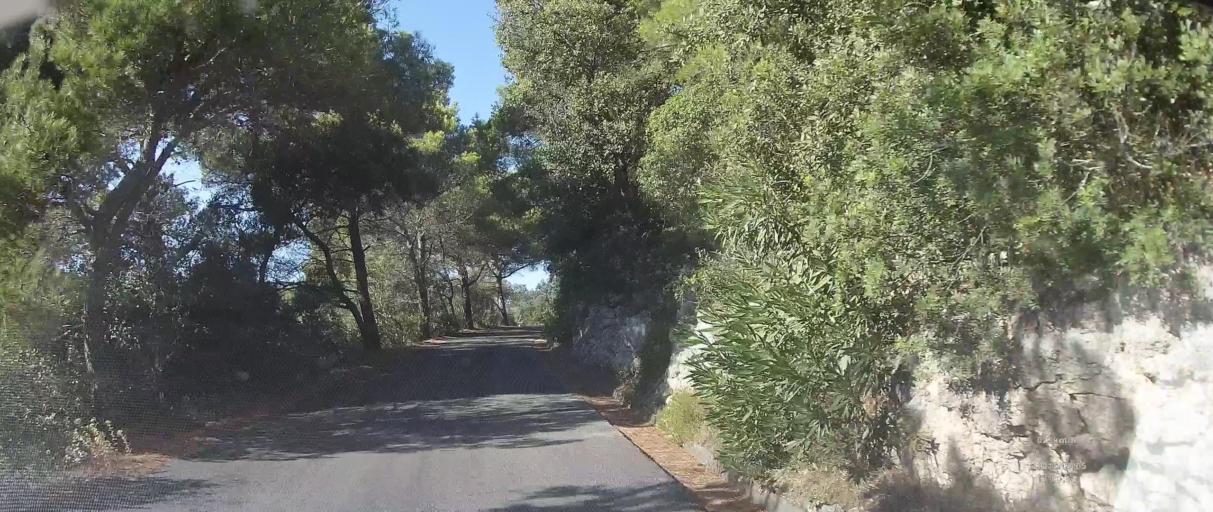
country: HR
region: Dubrovacko-Neretvanska
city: Blato
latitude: 42.7811
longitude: 17.3665
